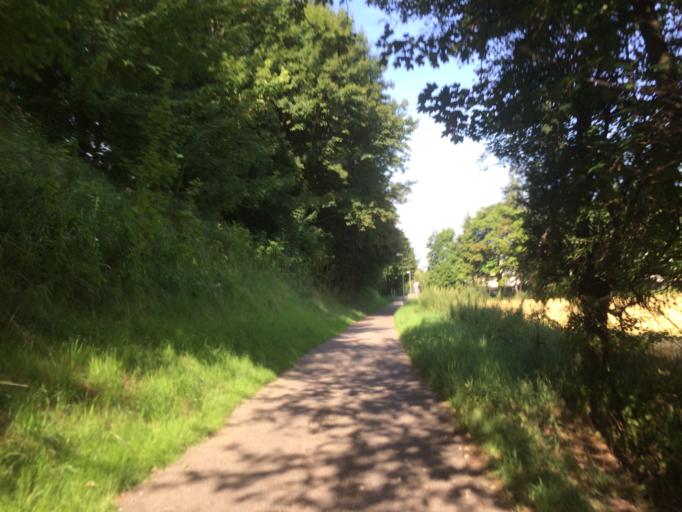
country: DE
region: Bavaria
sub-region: Swabia
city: Friedberg
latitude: 48.3514
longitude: 10.9757
